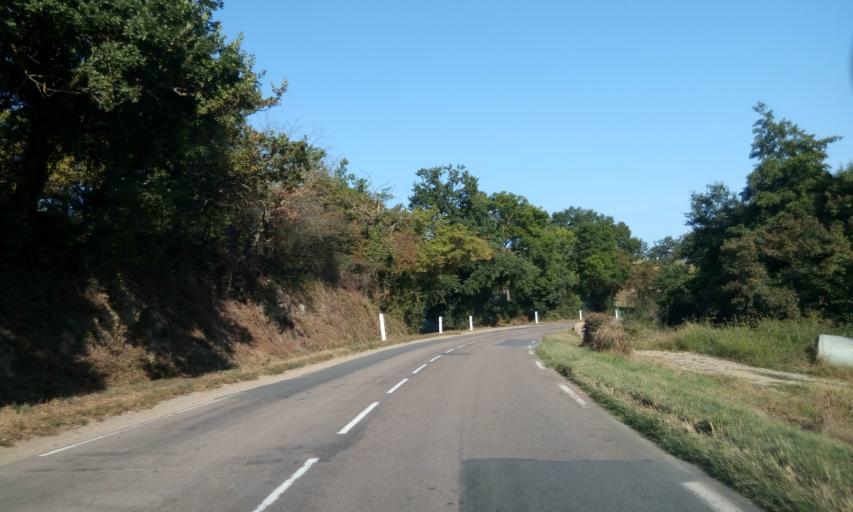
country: FR
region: Rhone-Alpes
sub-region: Departement du Rhone
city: Saint-Verand
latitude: 45.9036
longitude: 4.5446
